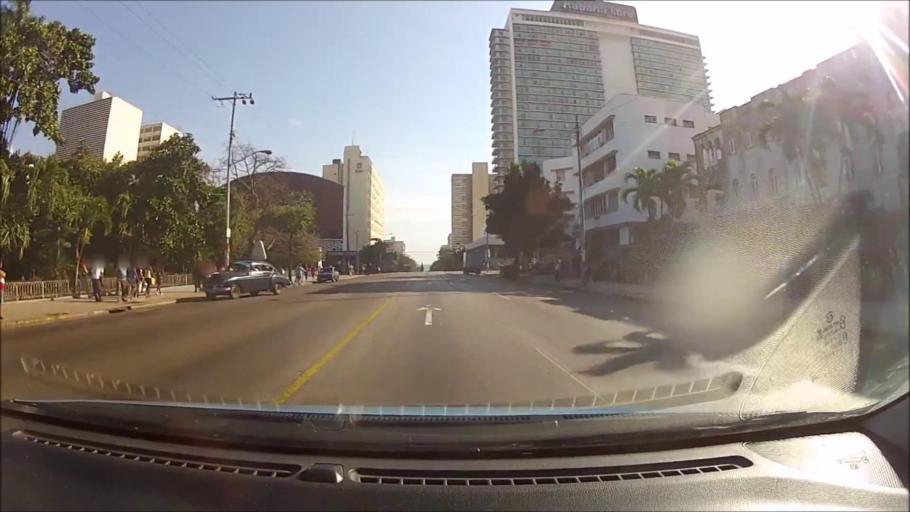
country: CU
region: La Habana
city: Havana
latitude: 23.1379
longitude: -82.3856
